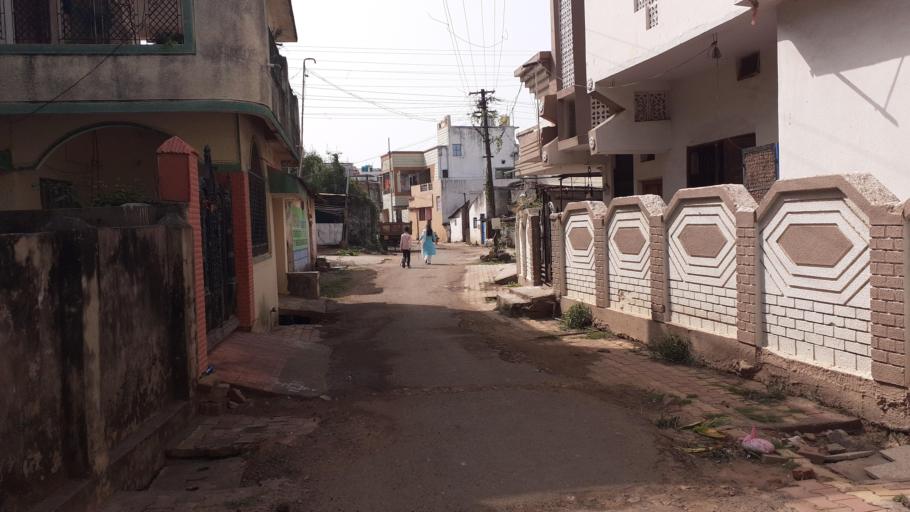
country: IN
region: Maharashtra
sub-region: Chandrapur
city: Ghugus
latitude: 20.1068
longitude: 79.1118
